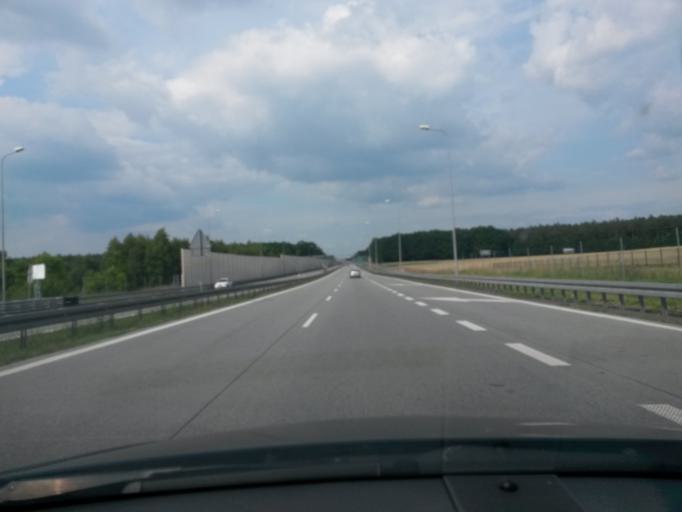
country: PL
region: Lodz Voivodeship
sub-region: Powiat rawski
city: Rawa Mazowiecka
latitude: 51.8042
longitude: 20.3014
